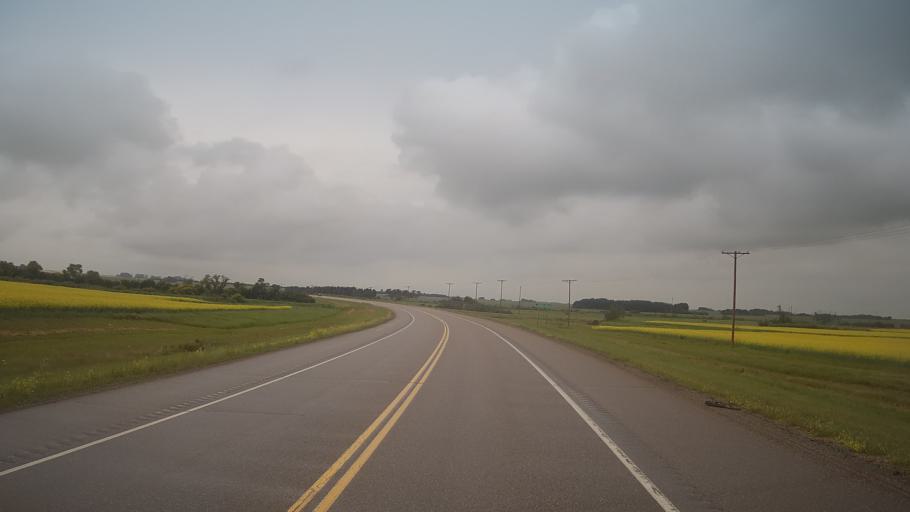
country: CA
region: Saskatchewan
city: Wilkie
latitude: 52.4333
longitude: -108.9264
